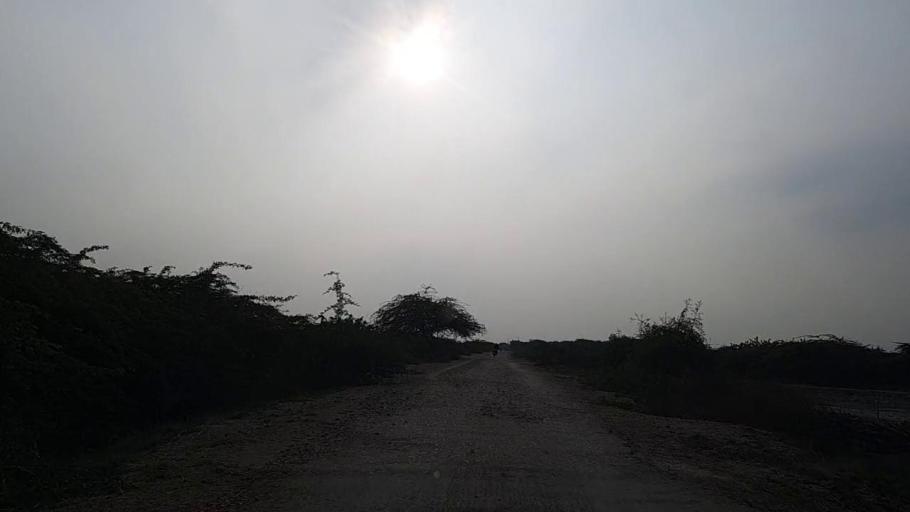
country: PK
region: Sindh
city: Mirpur Sakro
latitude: 24.6093
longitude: 67.5304
